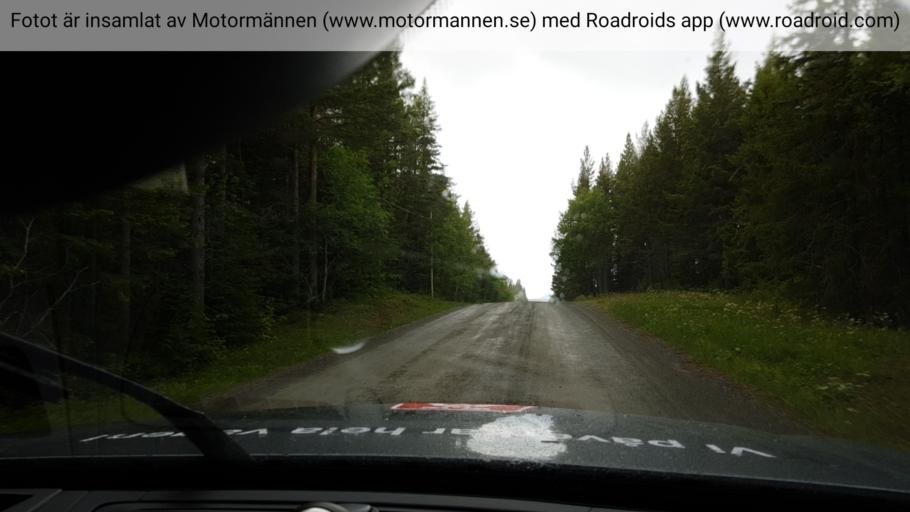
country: SE
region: Jaemtland
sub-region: Bergs Kommun
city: Hoverberg
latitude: 62.9860
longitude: 14.1860
